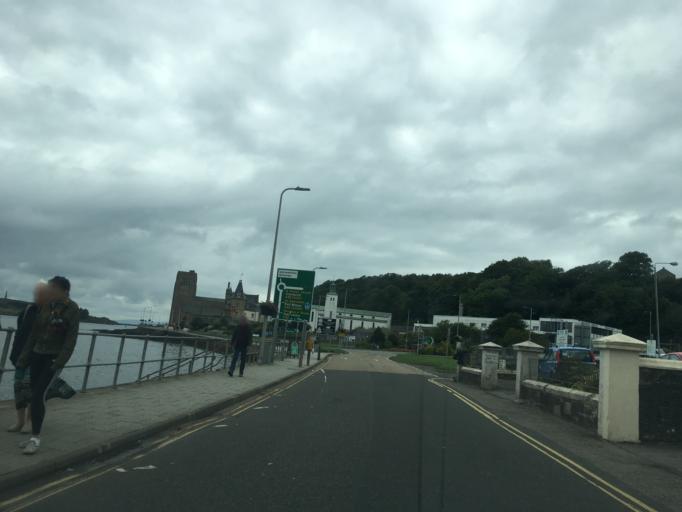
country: GB
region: Scotland
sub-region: Argyll and Bute
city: Oban
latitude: 56.4175
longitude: -5.4749
